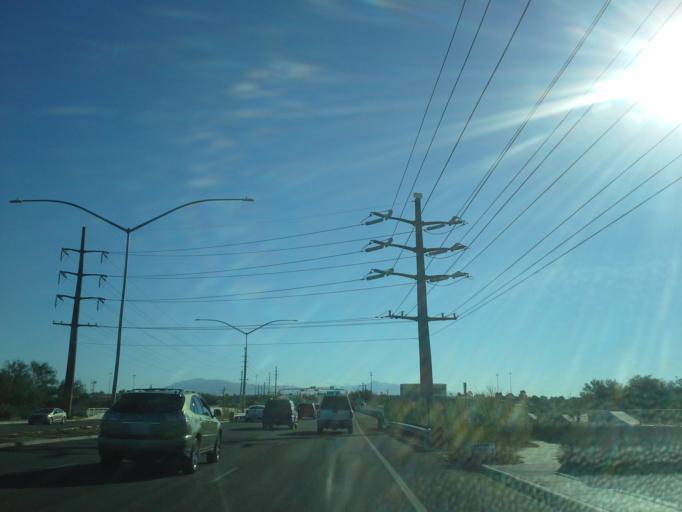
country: US
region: Arizona
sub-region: Pima County
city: Drexel Heights
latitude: 32.1336
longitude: -110.9942
